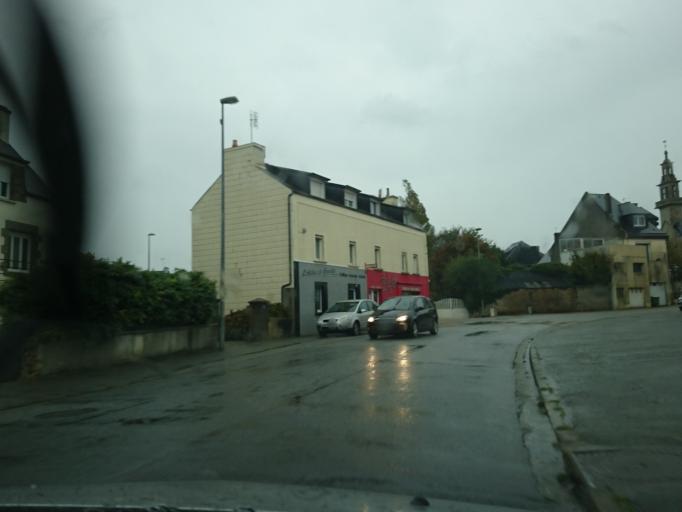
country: FR
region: Brittany
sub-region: Departement du Finistere
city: Plouvien
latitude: 48.5292
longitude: -4.4525
